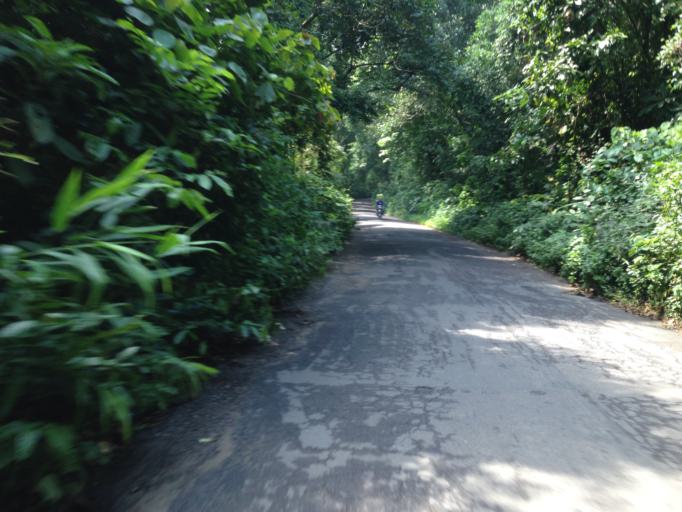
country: IN
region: Tripura
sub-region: Dhalai
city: Kamalpur
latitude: 24.3161
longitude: 91.7761
